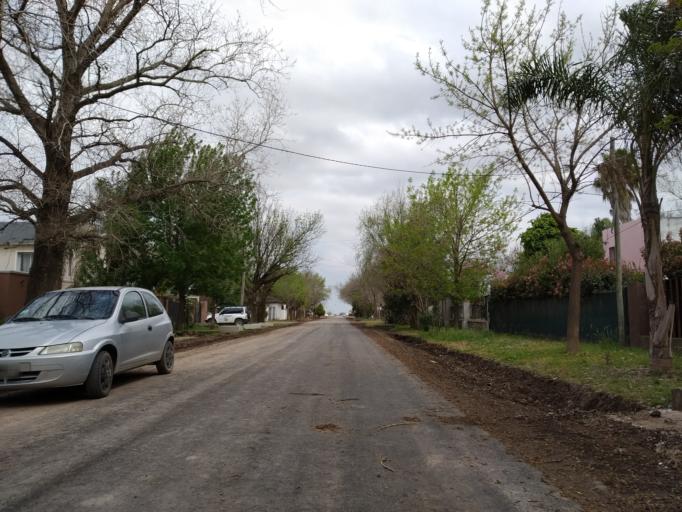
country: AR
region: Santa Fe
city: Funes
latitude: -32.9229
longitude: -60.8511
